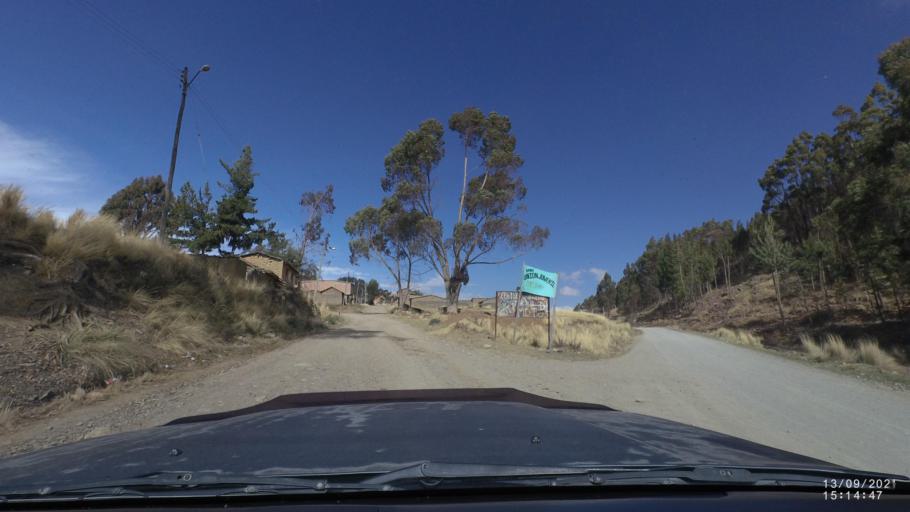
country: BO
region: Cochabamba
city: Colomi
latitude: -17.3670
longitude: -65.7976
